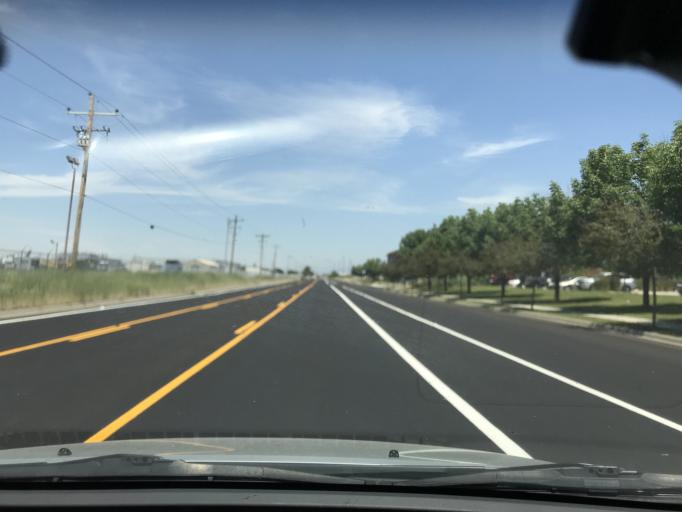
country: US
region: Utah
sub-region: Salt Lake County
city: Salt Lake City
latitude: 40.7902
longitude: -111.9535
